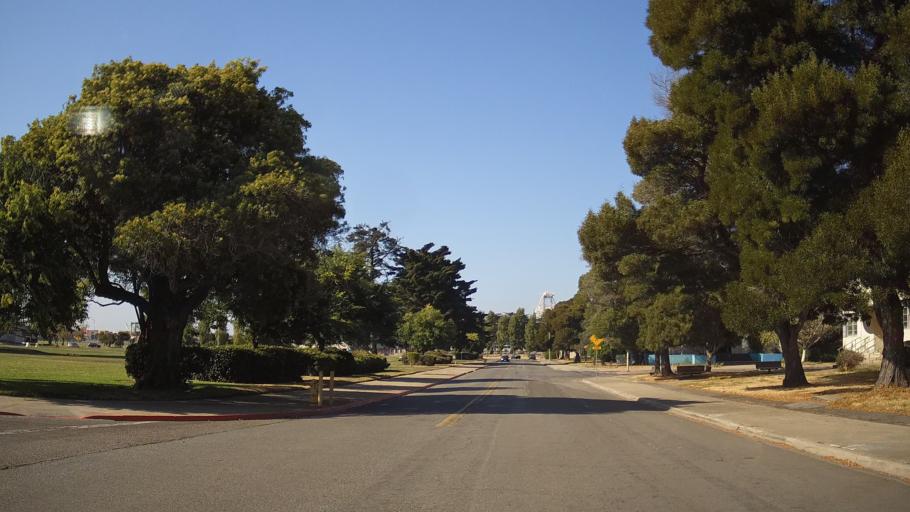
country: US
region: California
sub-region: Alameda County
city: Oakland
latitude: 37.7867
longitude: -122.3022
